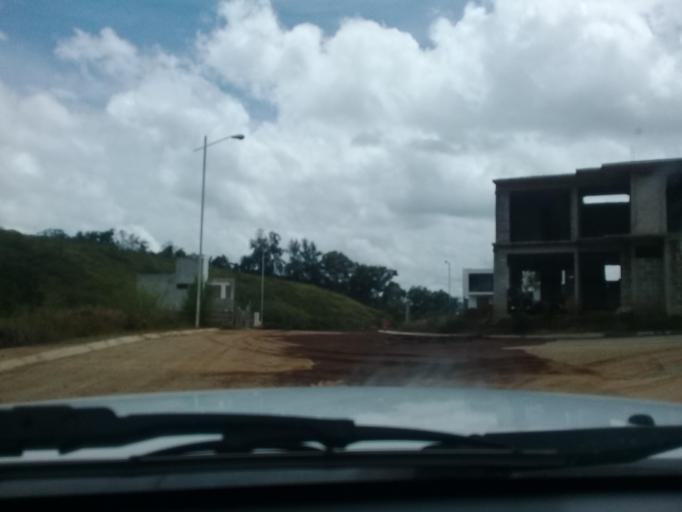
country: MX
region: Veracruz
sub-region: Xalapa
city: Lomas Verdes
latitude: 19.4988
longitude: -96.9130
